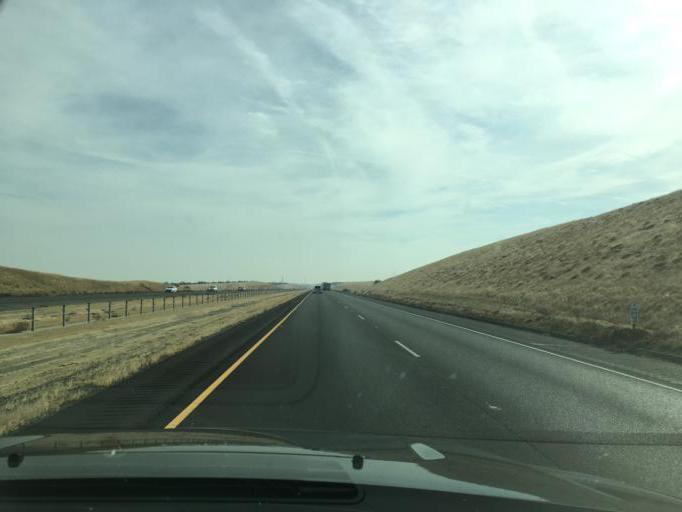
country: US
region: California
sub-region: Kings County
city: Kettleman City
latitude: 36.0430
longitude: -120.0457
